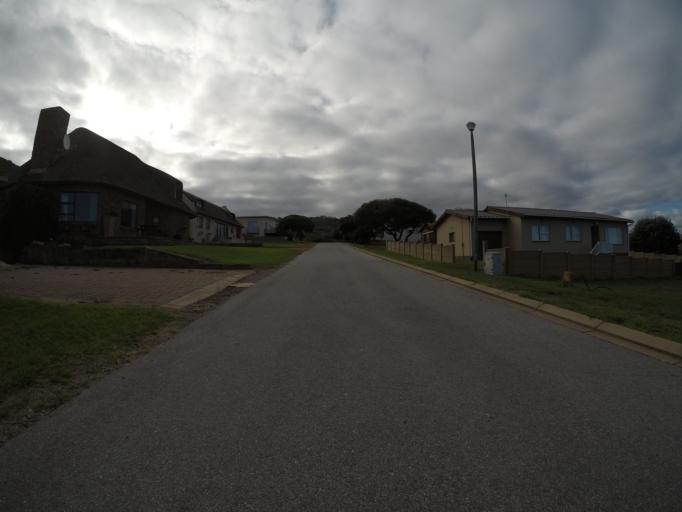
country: ZA
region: Western Cape
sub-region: Eden District Municipality
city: Riversdale
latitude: -34.4266
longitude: 21.3352
